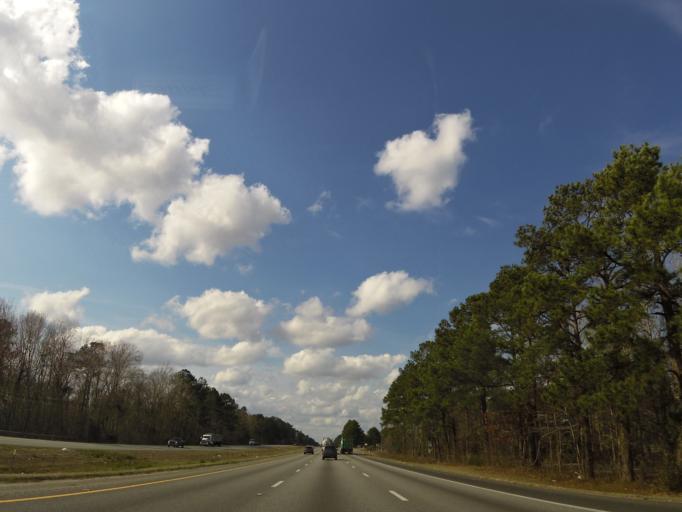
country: US
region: South Carolina
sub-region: Berkeley County
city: Ladson
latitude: 33.0074
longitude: -80.1057
